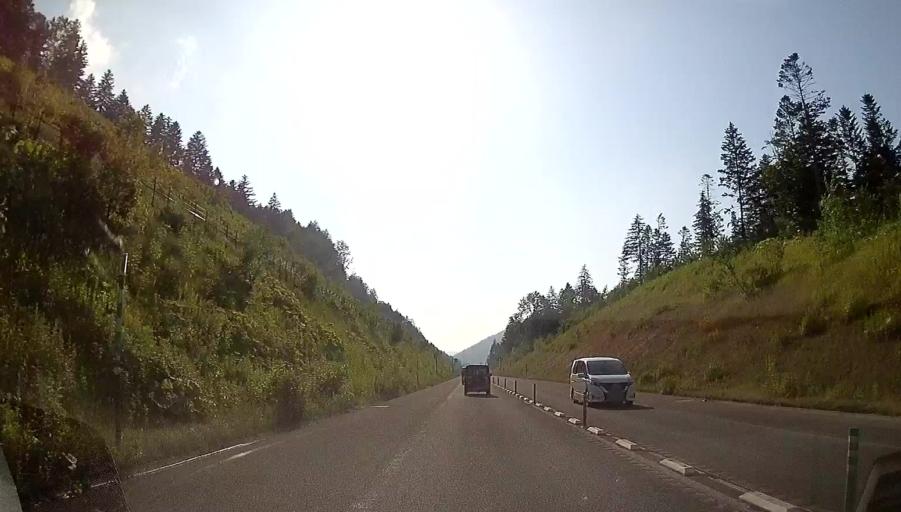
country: JP
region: Hokkaido
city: Shimo-furano
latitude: 43.0521
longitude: 142.6217
